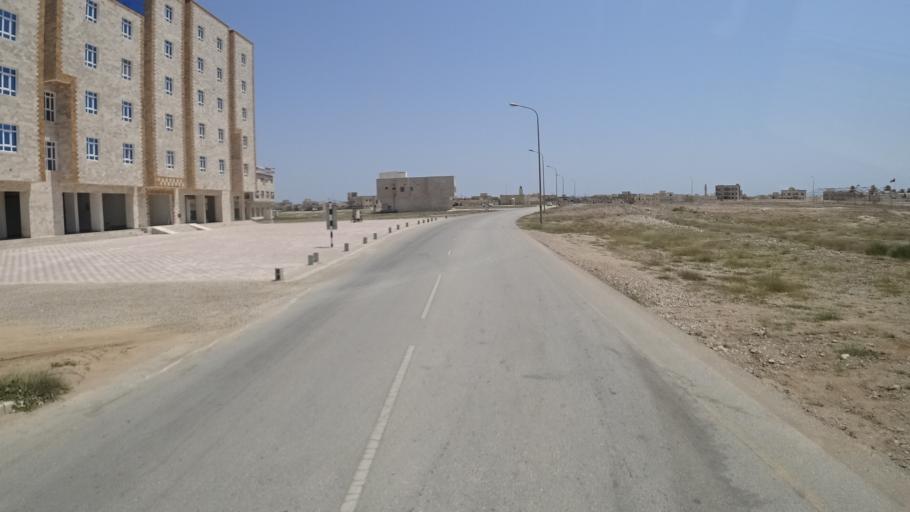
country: OM
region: Zufar
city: Salalah
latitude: 16.9958
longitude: 54.6962
